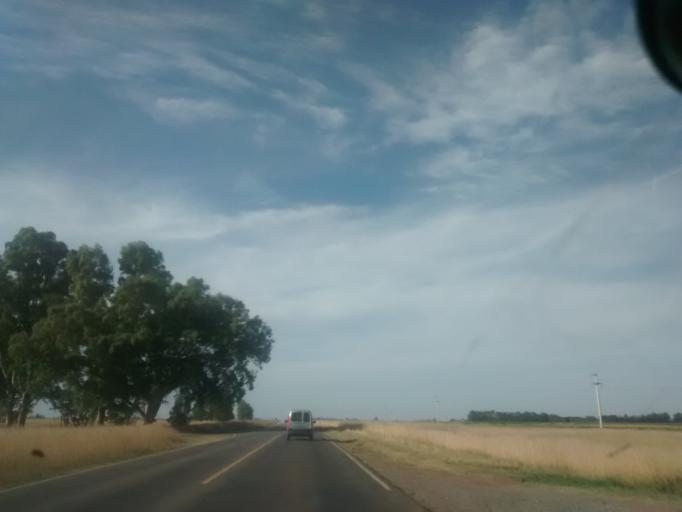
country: AR
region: Buenos Aires
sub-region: Partido de Ayacucho
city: Ayacucho
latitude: -37.1209
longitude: -58.5505
